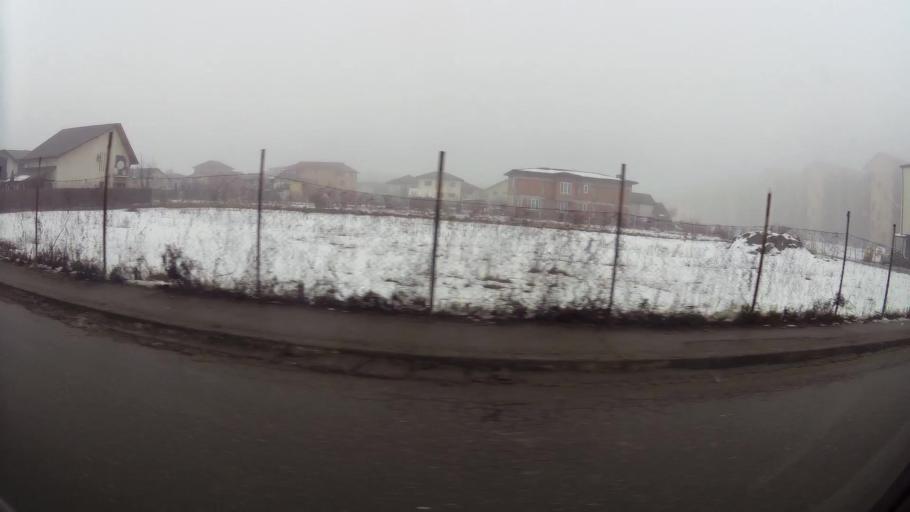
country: RO
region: Ilfov
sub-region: Comuna Chiajna
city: Chiajna
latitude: 44.4483
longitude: 25.9818
